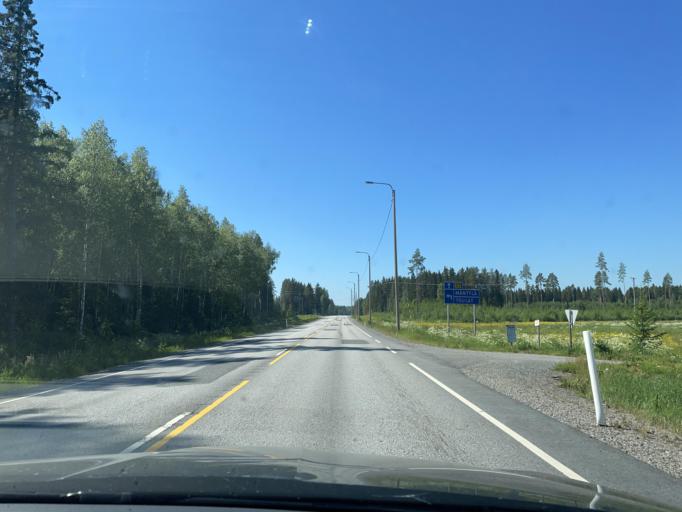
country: FI
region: Central Finland
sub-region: Saarijaervi-Viitasaari
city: Viitasaari
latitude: 63.1742
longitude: 26.0179
